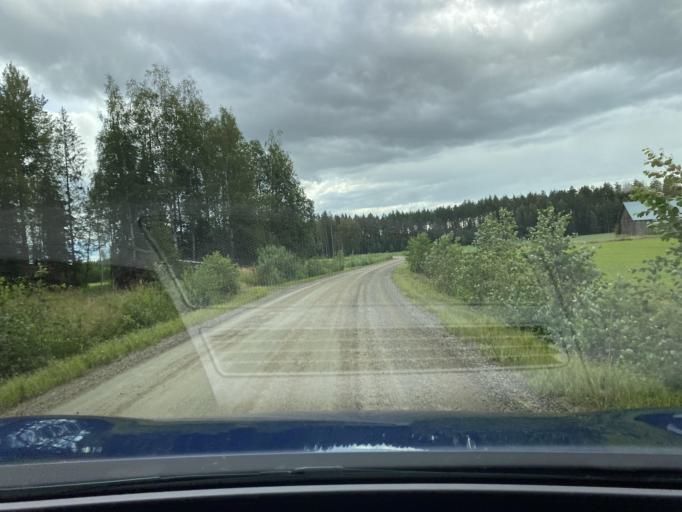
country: FI
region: Pirkanmaa
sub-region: Lounais-Pirkanmaa
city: Punkalaidun
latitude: 61.2051
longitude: 23.1781
